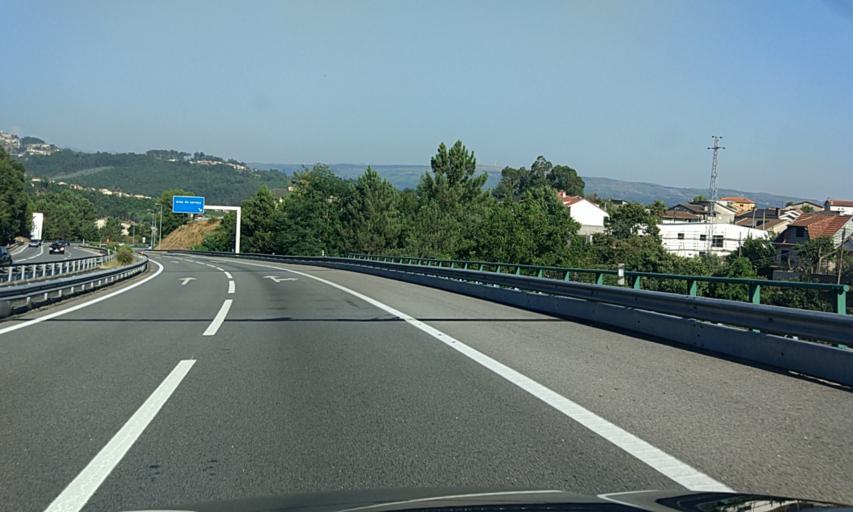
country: PT
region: Porto
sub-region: Marco de Canaveses
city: Marco de Canavezes
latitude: 41.2339
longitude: -8.1891
